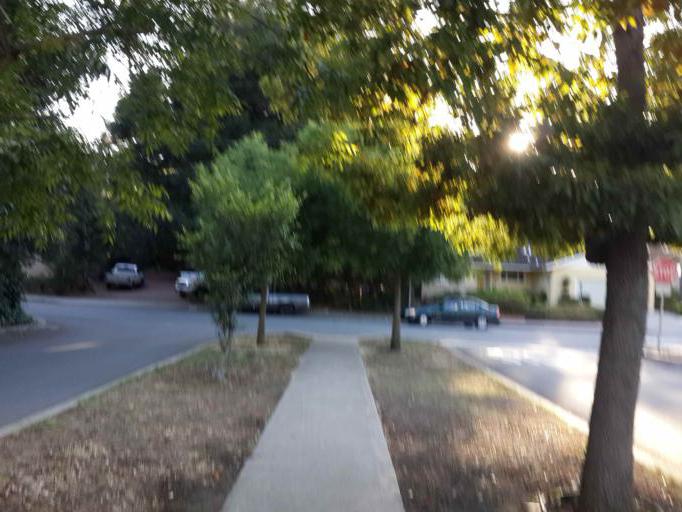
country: US
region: California
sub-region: San Luis Obispo County
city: San Luis Obispo
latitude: 35.2908
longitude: -120.6714
